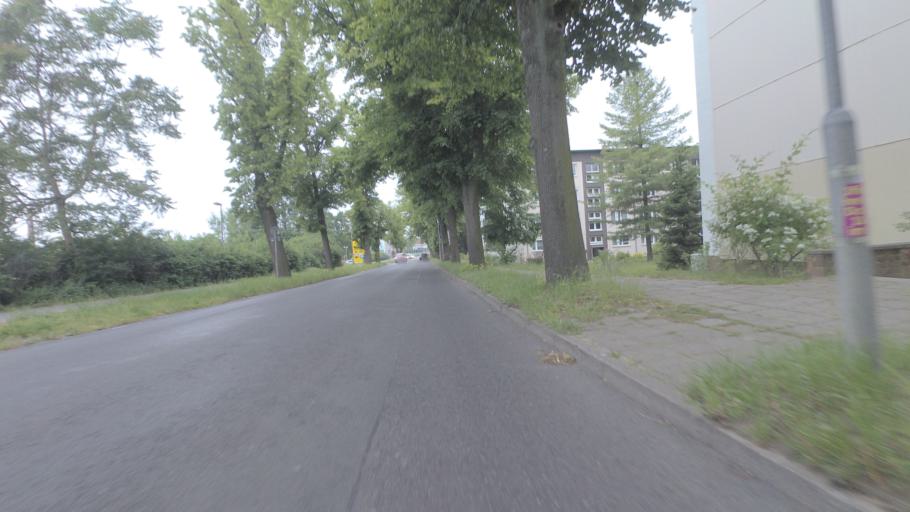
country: DE
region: Brandenburg
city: Rangsdorf
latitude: 52.2957
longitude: 13.4354
